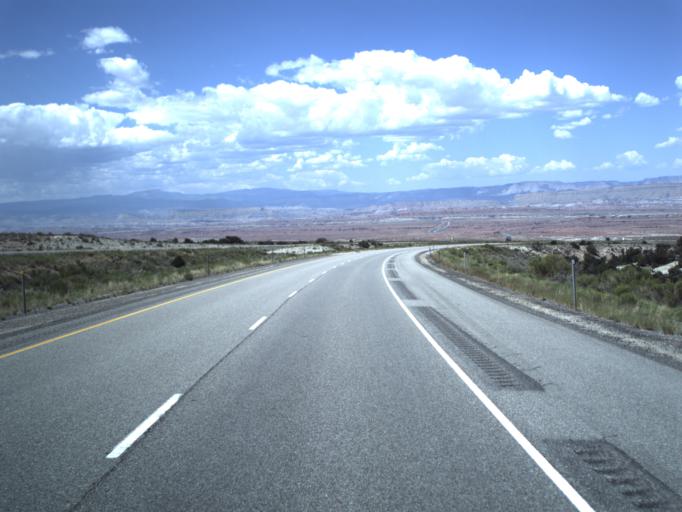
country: US
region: Utah
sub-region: Emery County
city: Ferron
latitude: 38.8417
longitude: -110.9574
